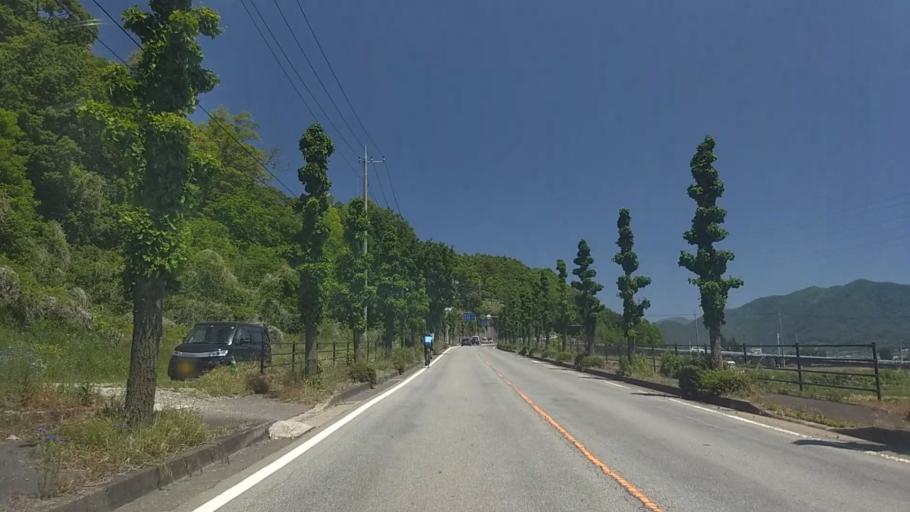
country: JP
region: Yamanashi
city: Nirasaki
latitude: 35.7993
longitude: 138.4249
